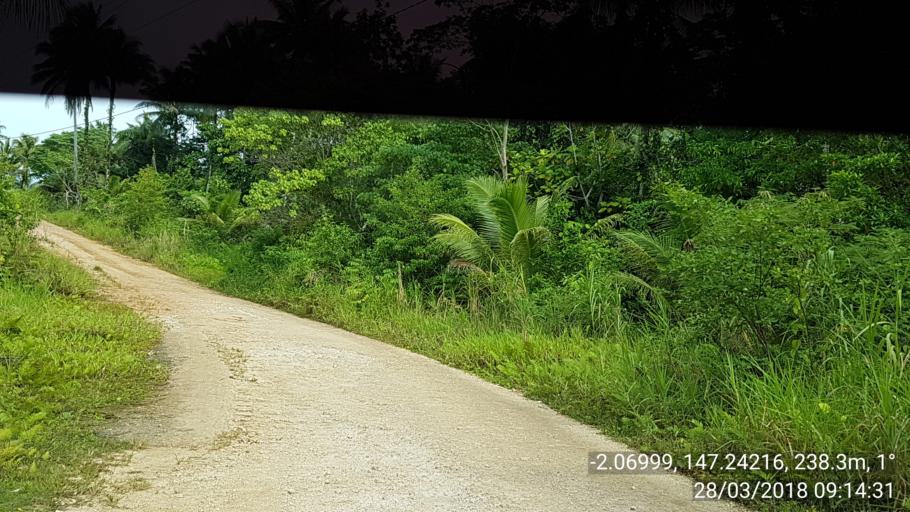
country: PG
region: Manus
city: Lorengau
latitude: -2.0700
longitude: 147.2422
